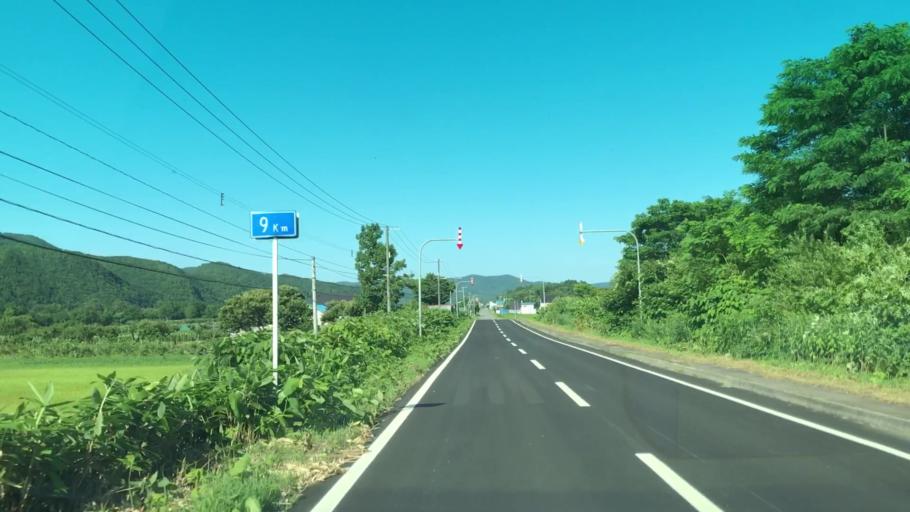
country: JP
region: Hokkaido
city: Yoichi
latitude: 43.0340
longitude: 140.7771
